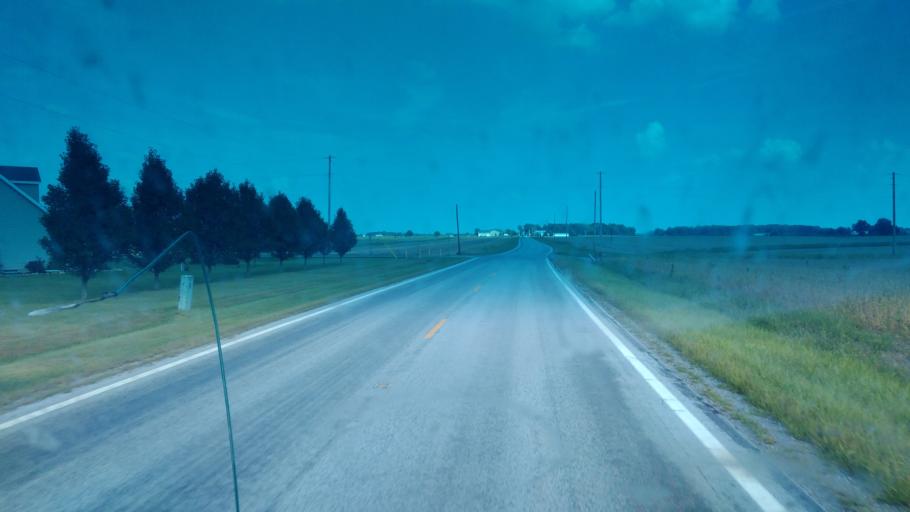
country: US
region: Ohio
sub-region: Hardin County
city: Forest
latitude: 40.8910
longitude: -83.5389
